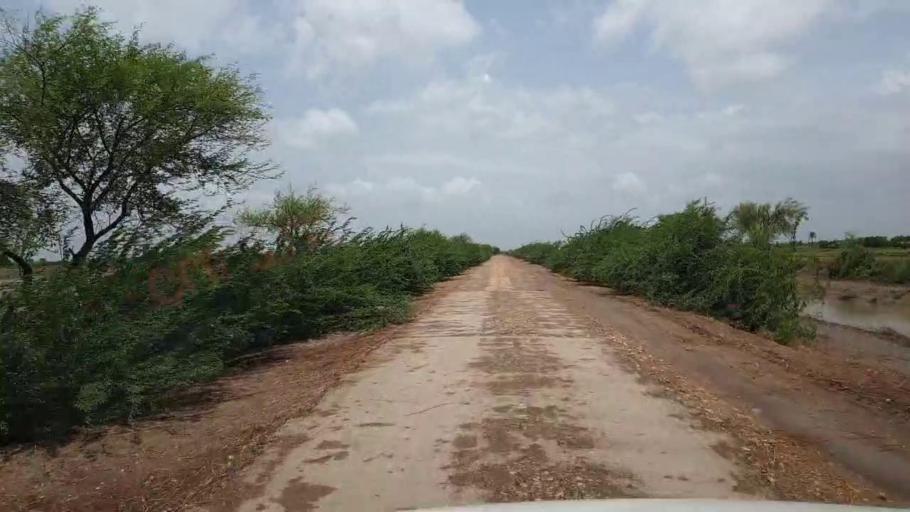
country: PK
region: Sindh
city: Kario
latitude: 24.7109
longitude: 68.5979
